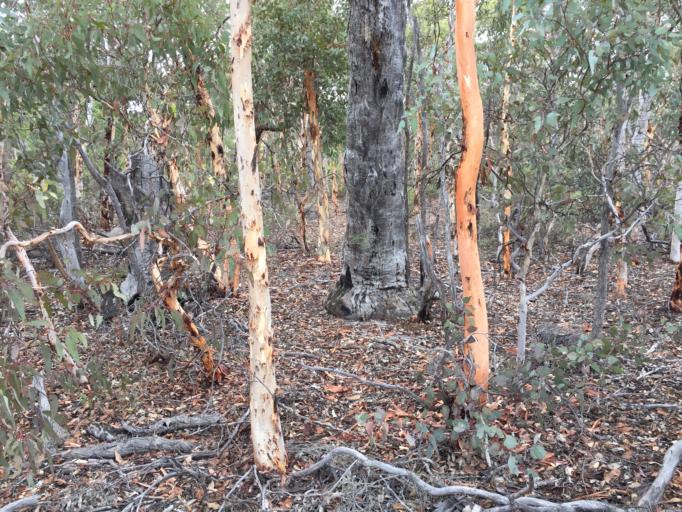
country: AU
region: Western Australia
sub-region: Narrogin
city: Narrogin
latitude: -32.7970
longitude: 116.9431
